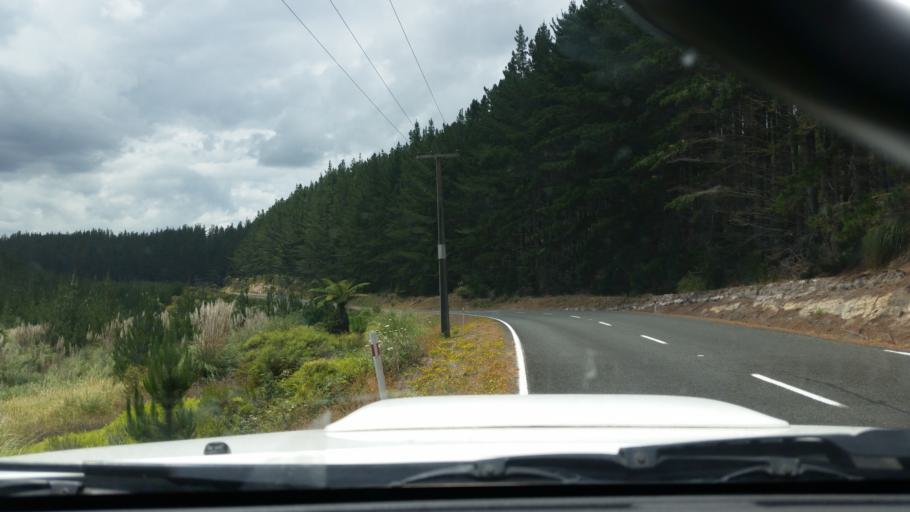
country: NZ
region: Northland
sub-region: Kaipara District
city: Dargaville
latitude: -35.8225
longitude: 173.7016
